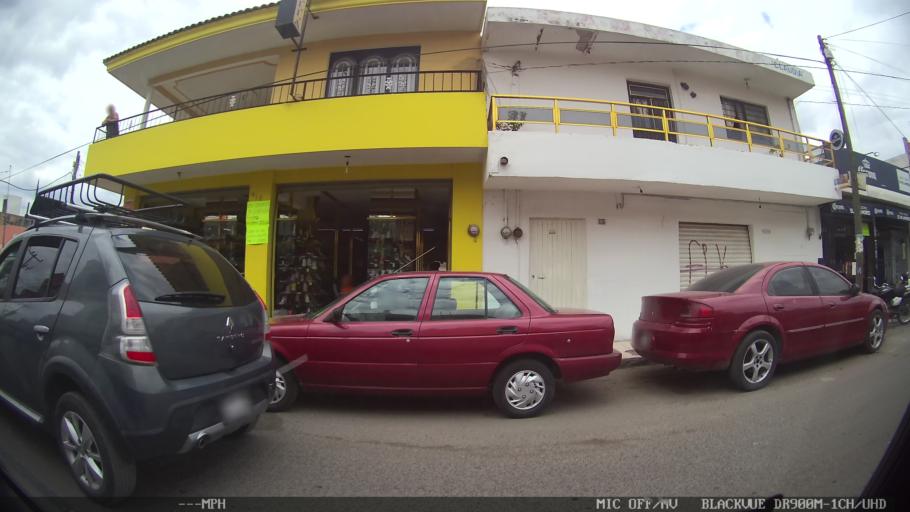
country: MX
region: Jalisco
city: Tonala
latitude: 20.6532
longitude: -103.2540
